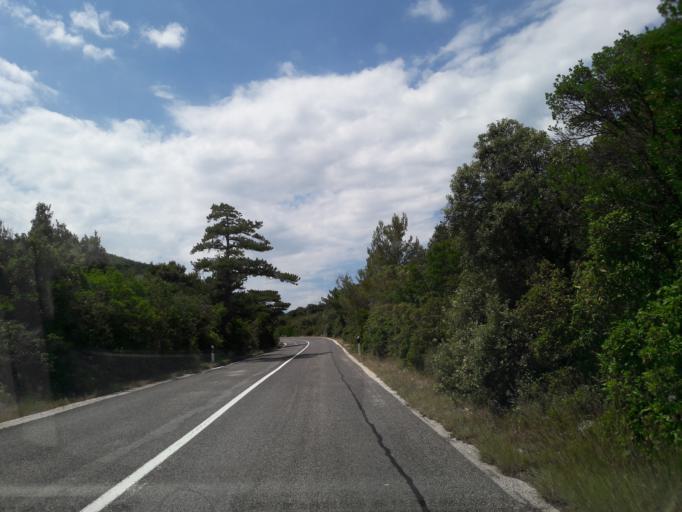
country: HR
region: Dubrovacko-Neretvanska
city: Orebic
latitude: 42.9691
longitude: 17.2836
